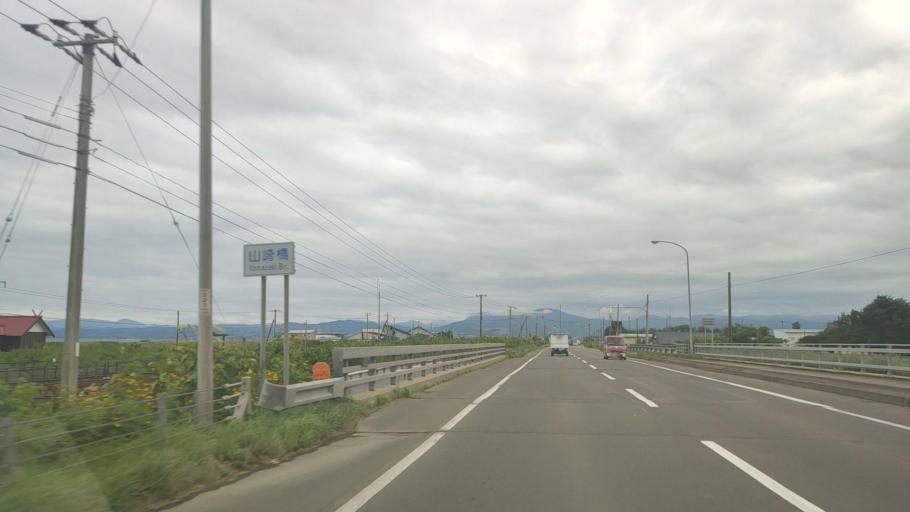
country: JP
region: Hokkaido
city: Nanae
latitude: 42.3210
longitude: 140.2755
